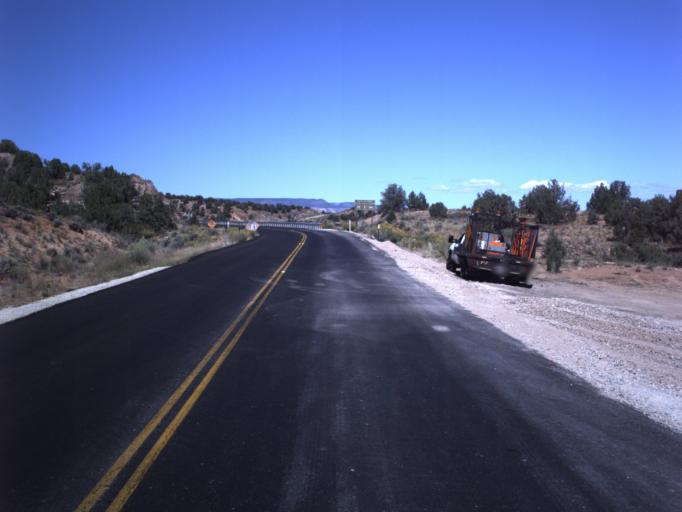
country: US
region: Utah
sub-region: San Juan County
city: Blanding
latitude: 37.5607
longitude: -109.5797
